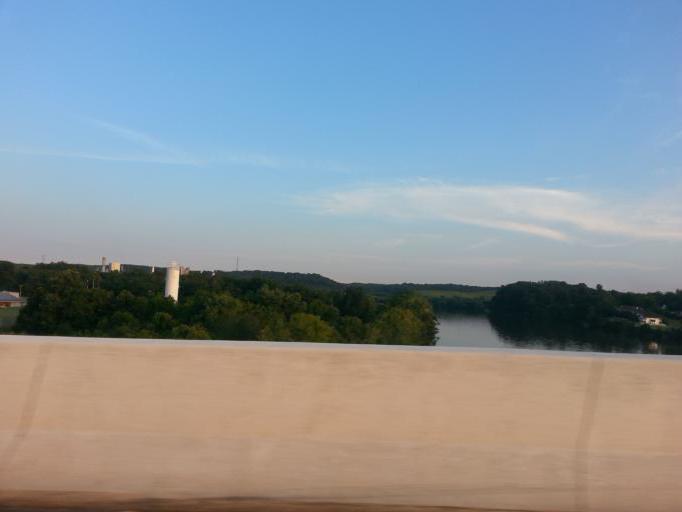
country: US
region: Tennessee
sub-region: Loudon County
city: Loudon
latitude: 35.7432
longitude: -84.3299
